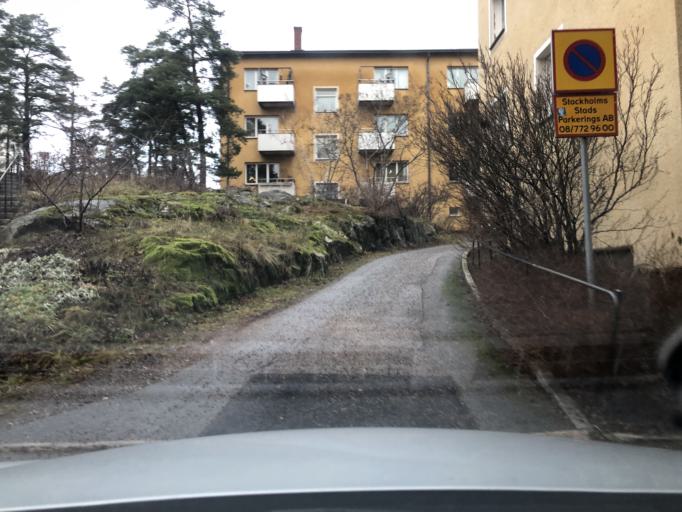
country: SE
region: Stockholm
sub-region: Stockholms Kommun
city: Arsta
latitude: 59.2996
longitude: 18.0504
